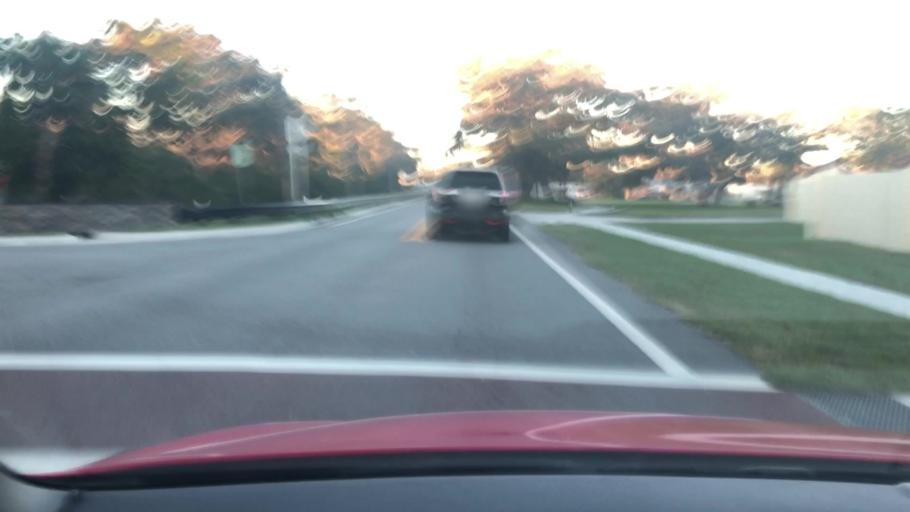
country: US
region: Florida
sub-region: Volusia County
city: South Daytona
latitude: 29.1585
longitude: -81.0067
